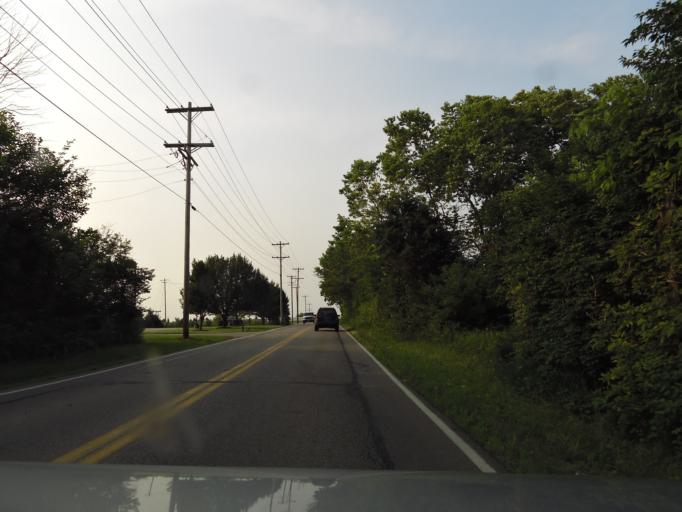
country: US
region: Ohio
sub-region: Butler County
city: Hamilton
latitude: 39.3845
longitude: -84.5154
